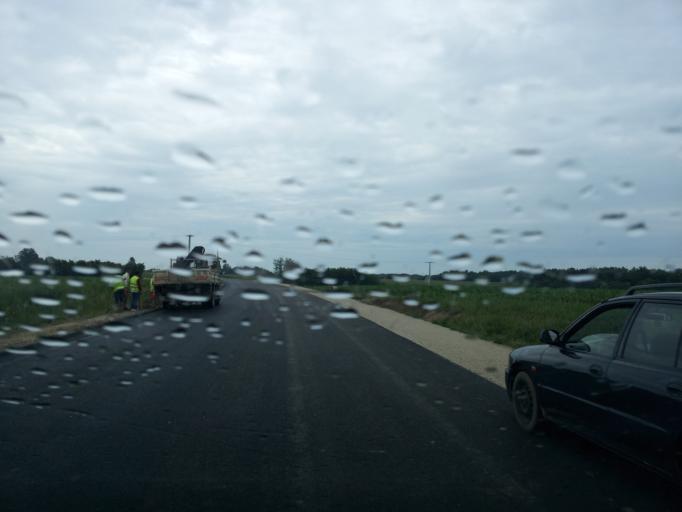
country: HU
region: Vas
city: Kormend
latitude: 46.9568
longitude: 16.6360
